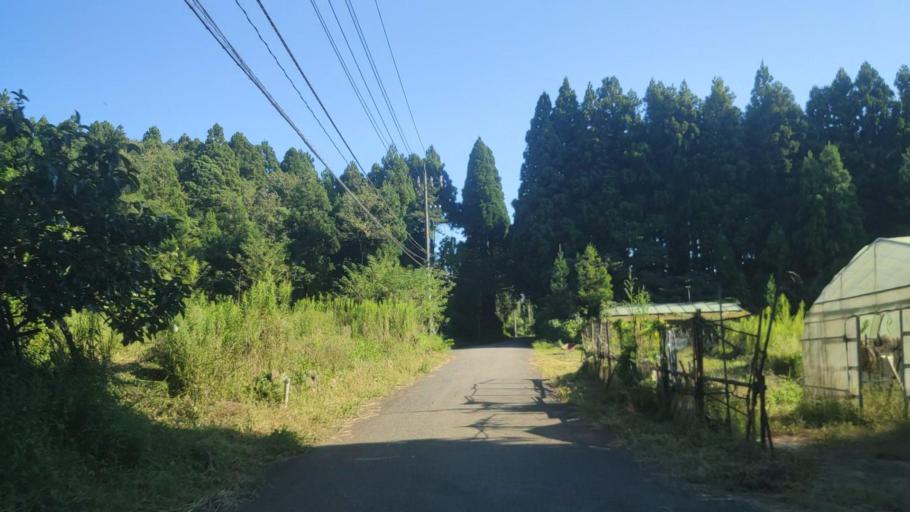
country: JP
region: Ishikawa
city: Nanao
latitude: 37.1356
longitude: 136.9092
